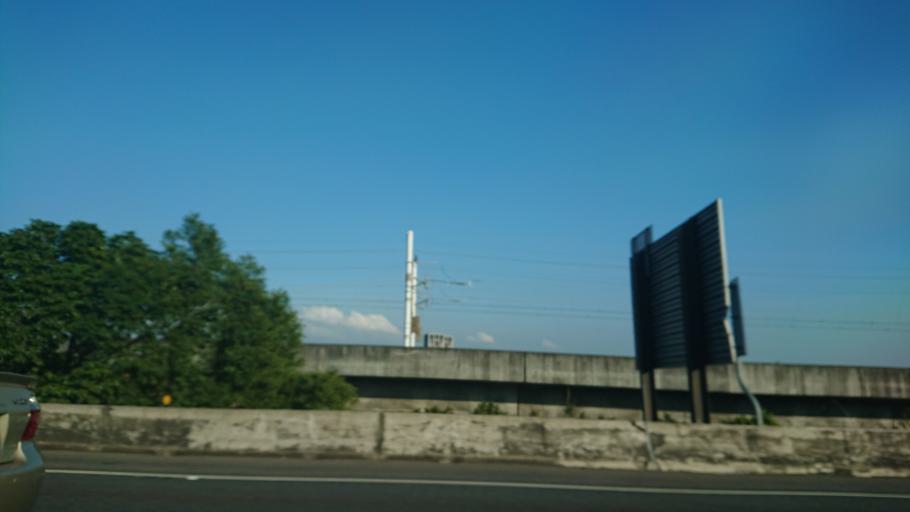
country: TW
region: Taiwan
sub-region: Taichung City
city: Taichung
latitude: 24.1377
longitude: 120.6179
